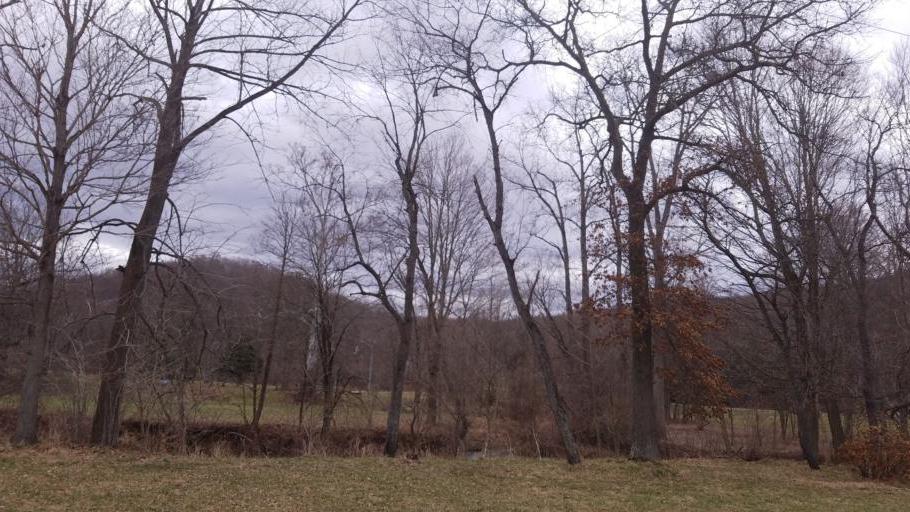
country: US
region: Ohio
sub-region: Licking County
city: Newark
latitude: 40.1658
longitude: -82.2934
